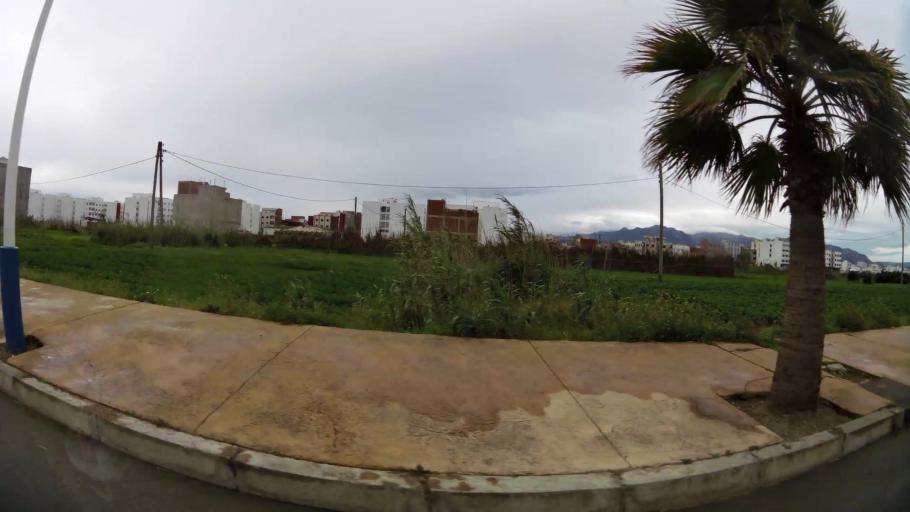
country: MA
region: Tanger-Tetouan
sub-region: Tetouan
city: Martil
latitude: 35.6301
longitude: -5.2898
